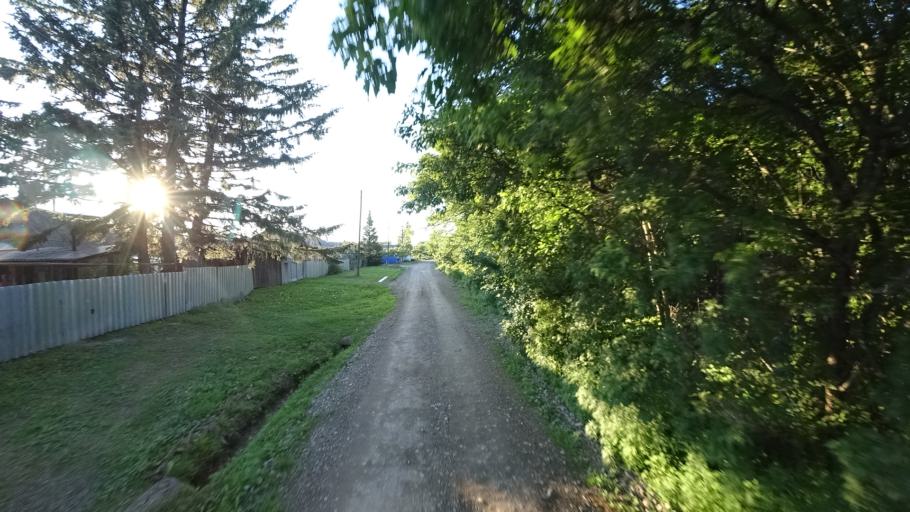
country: RU
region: Khabarovsk Krai
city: Khor
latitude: 47.8554
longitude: 135.0025
